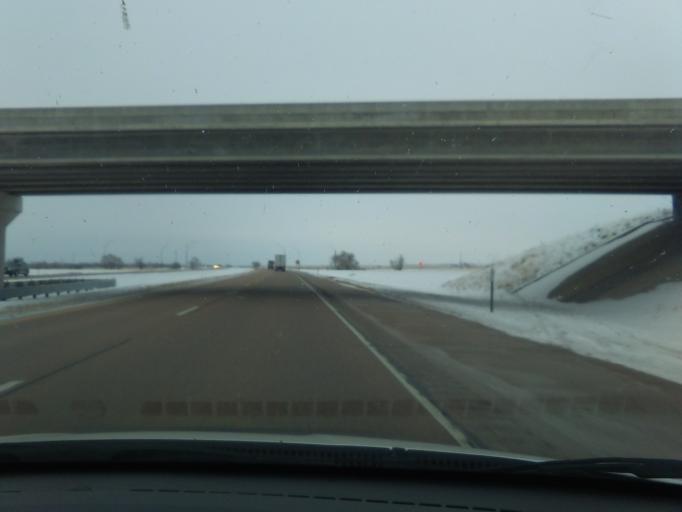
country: US
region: Nebraska
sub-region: Keith County
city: Ogallala
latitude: 41.0792
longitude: -101.8883
